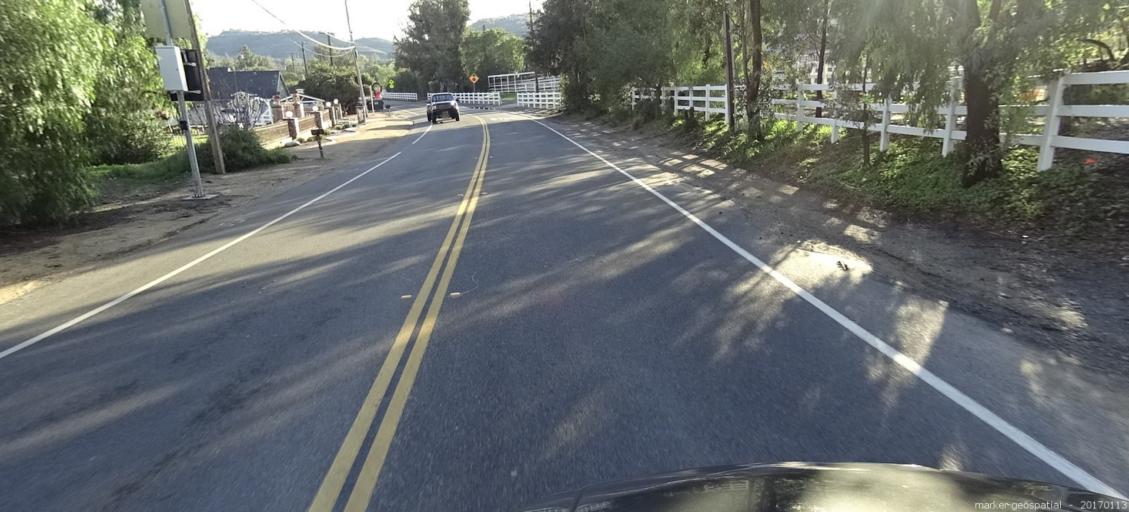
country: US
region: California
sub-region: Orange County
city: Villa Park
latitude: 33.8069
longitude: -117.7822
